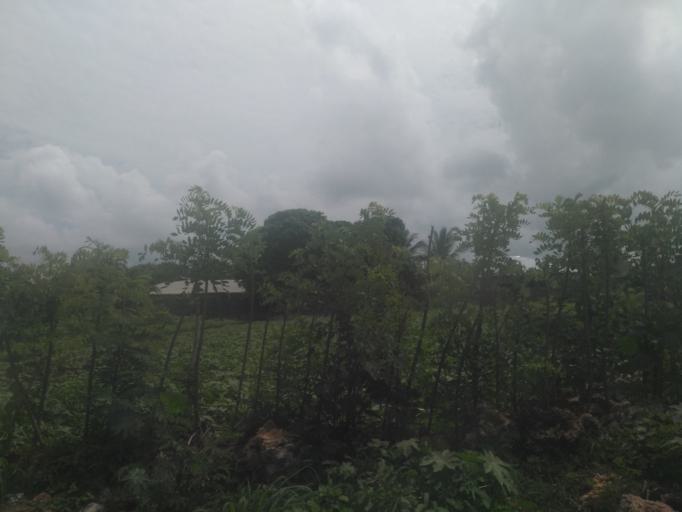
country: TZ
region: Zanzibar Urban/West
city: Zanzibar
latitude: -6.2260
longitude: 39.2142
